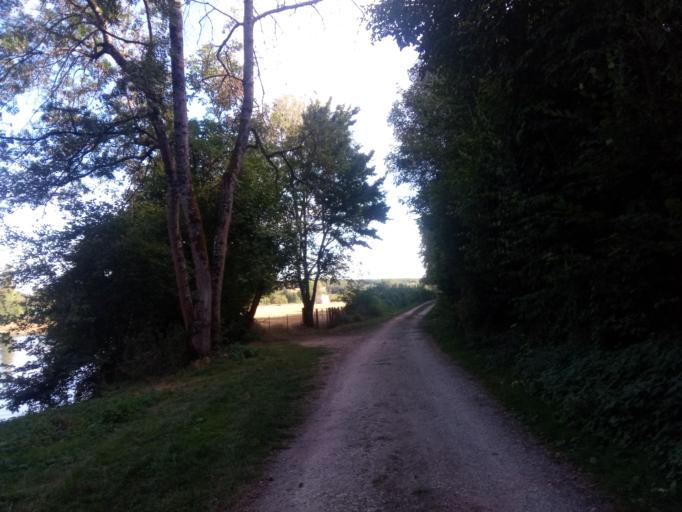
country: FR
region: Poitou-Charentes
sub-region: Departement de la Vienne
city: Saint-Savin
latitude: 46.5577
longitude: 0.8644
